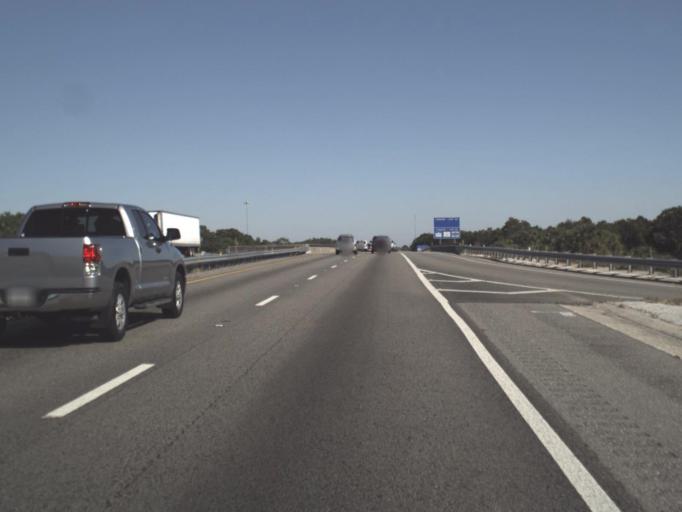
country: US
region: Florida
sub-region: Orange County
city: Williamsburg
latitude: 28.4210
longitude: -81.4440
